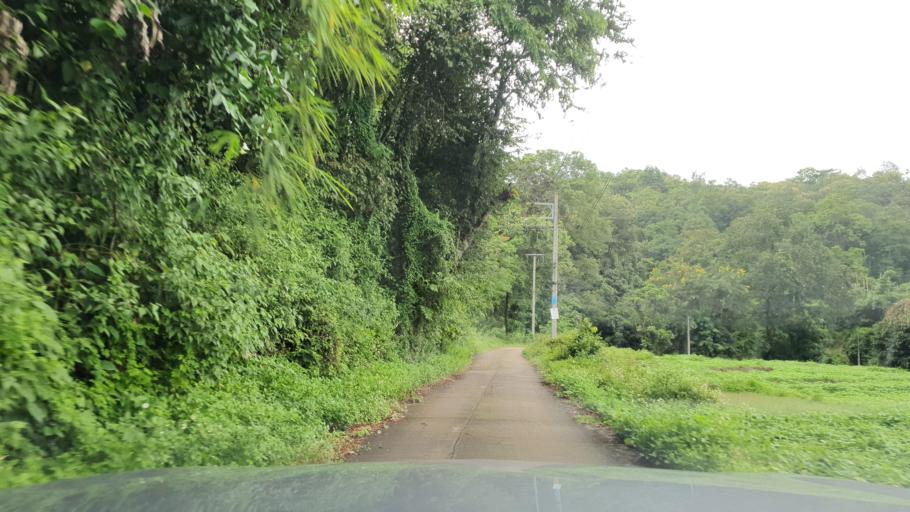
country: TH
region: Chiang Mai
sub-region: Amphoe Chiang Dao
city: Chiang Dao
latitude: 19.3381
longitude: 98.9266
